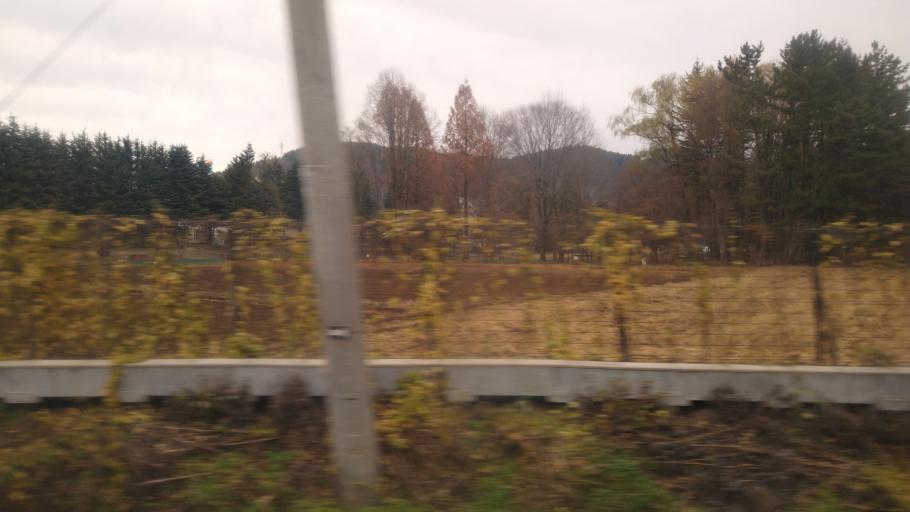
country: JP
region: Nagano
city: Shiojiri
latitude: 36.1094
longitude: 137.9435
